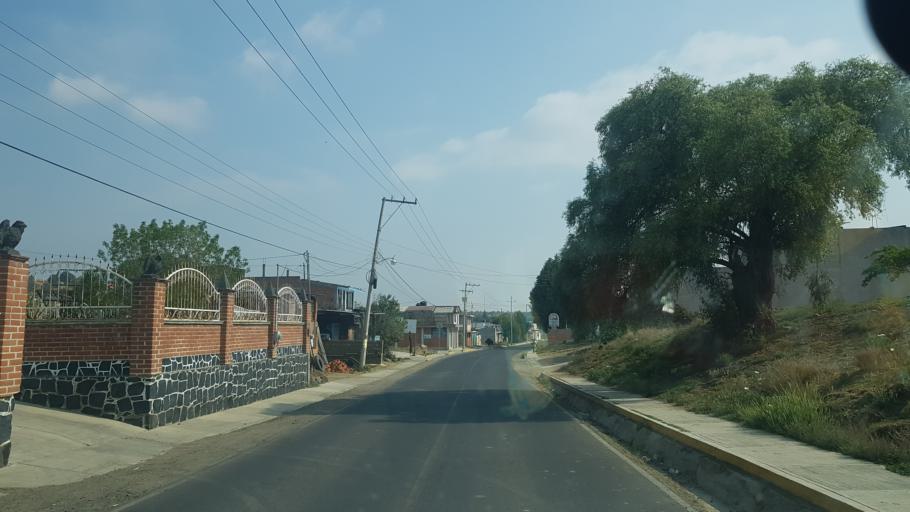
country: MX
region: Puebla
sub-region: Huejotzingo
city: San Juan Pancoac
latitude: 19.1180
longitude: -98.4252
